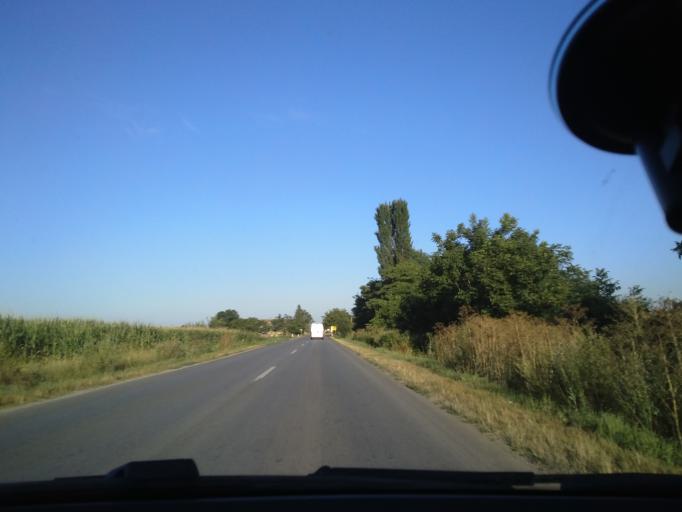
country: RS
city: Maglic
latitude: 45.3986
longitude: 19.4486
